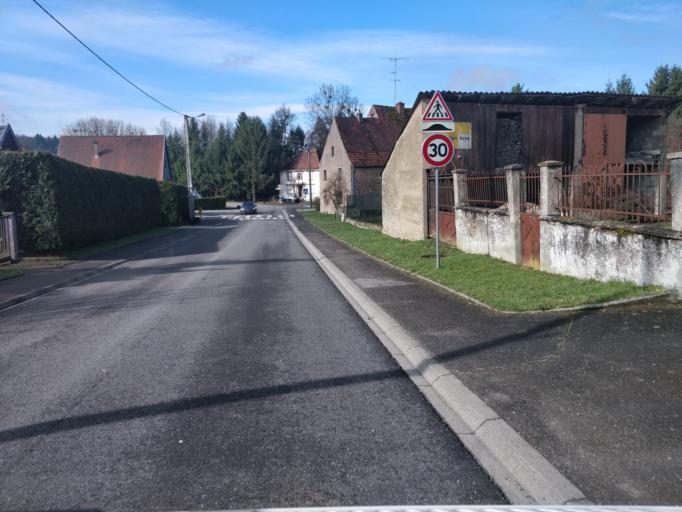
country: FR
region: Alsace
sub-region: Departement du Bas-Rhin
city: Drulingen
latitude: 48.8653
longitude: 7.2314
